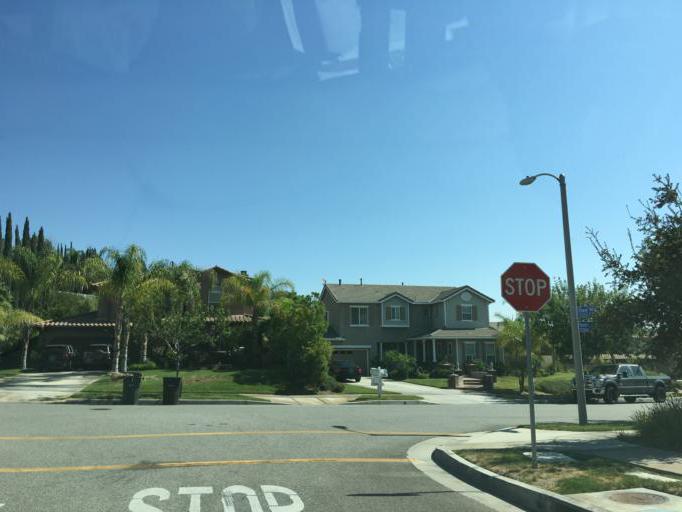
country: US
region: California
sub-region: Los Angeles County
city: Santa Clarita
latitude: 34.3849
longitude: -118.5779
